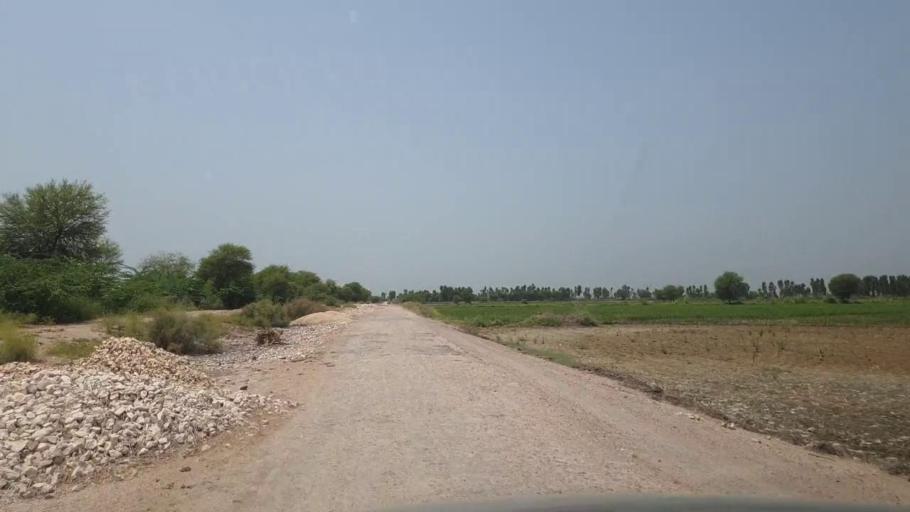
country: PK
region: Sindh
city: Garhi Yasin
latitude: 27.8856
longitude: 68.4360
